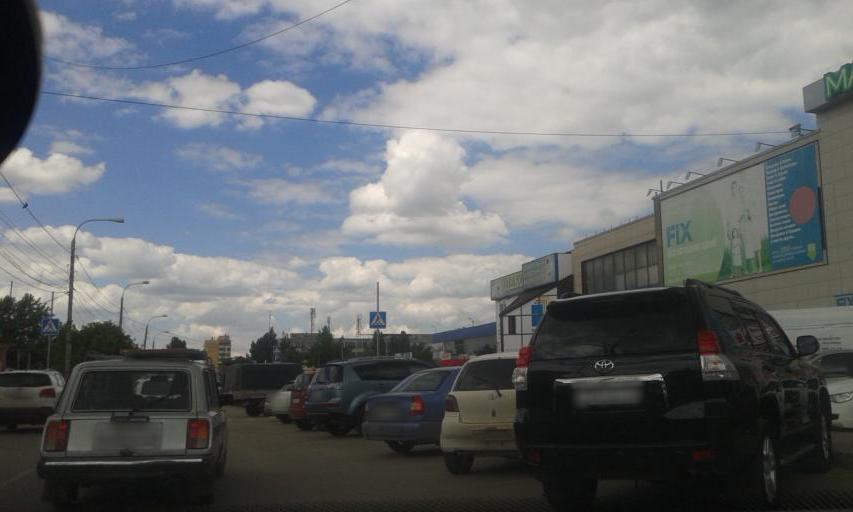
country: RU
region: Volgograd
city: Volgograd
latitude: 48.7576
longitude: 44.5015
